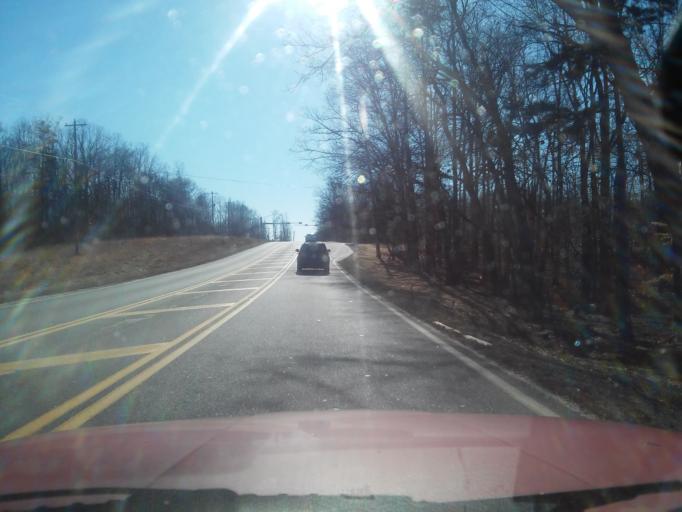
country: US
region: Virginia
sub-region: Fluvanna County
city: Palmyra
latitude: 37.9880
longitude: -78.2043
